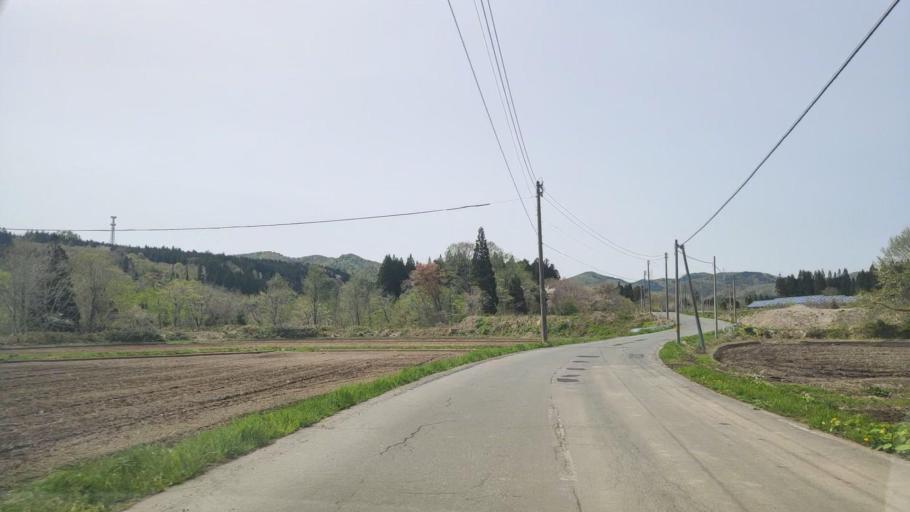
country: JP
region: Aomori
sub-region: Misawa Shi
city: Inuotose
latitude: 40.7827
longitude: 141.1186
